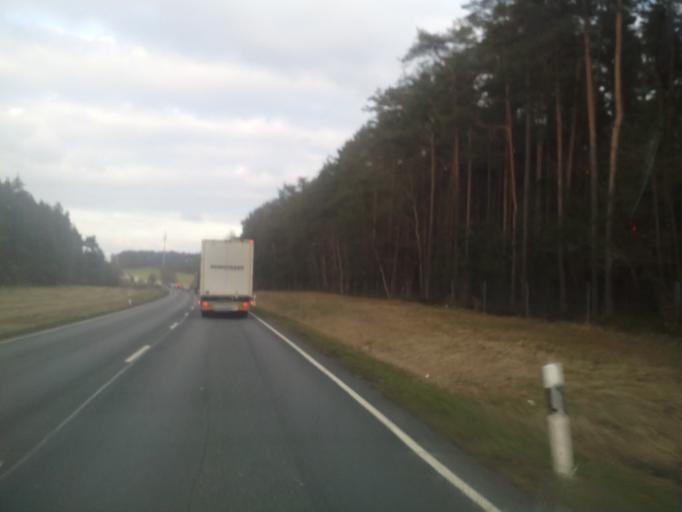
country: DE
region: Bavaria
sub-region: Regierungsbezirk Mittelfranken
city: Adelsdorf
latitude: 49.7594
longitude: 10.8701
